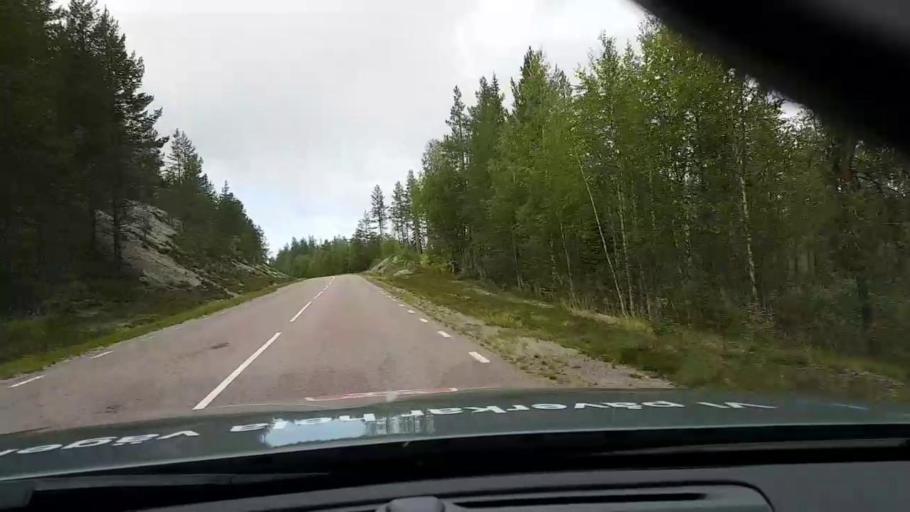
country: SE
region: Vaesterbotten
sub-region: Asele Kommun
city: Asele
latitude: 63.8772
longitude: 17.3566
